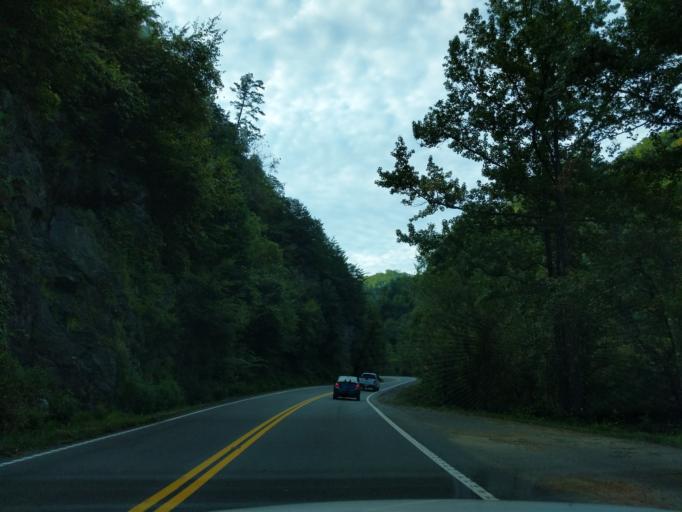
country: US
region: Tennessee
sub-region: Polk County
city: Benton
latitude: 35.0928
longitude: -84.5317
